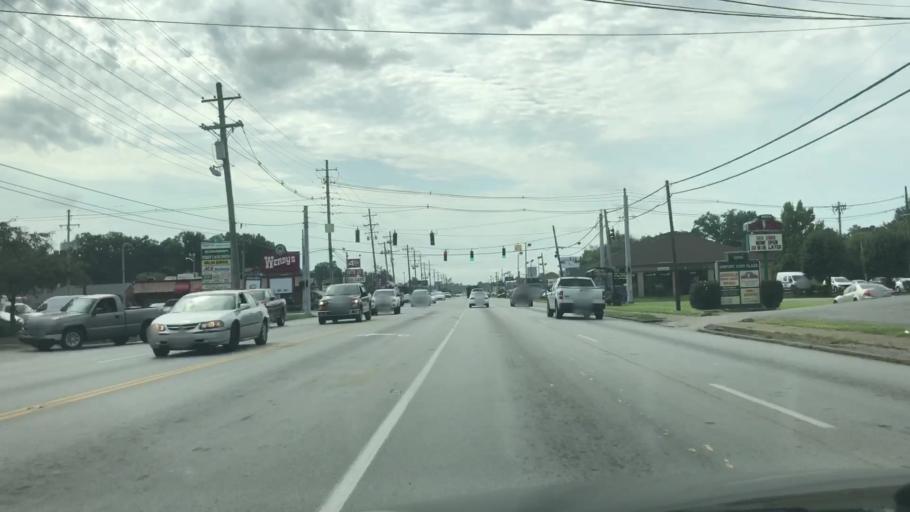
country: US
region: Kentucky
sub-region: Jefferson County
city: Audubon Park
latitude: 38.1752
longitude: -85.7134
